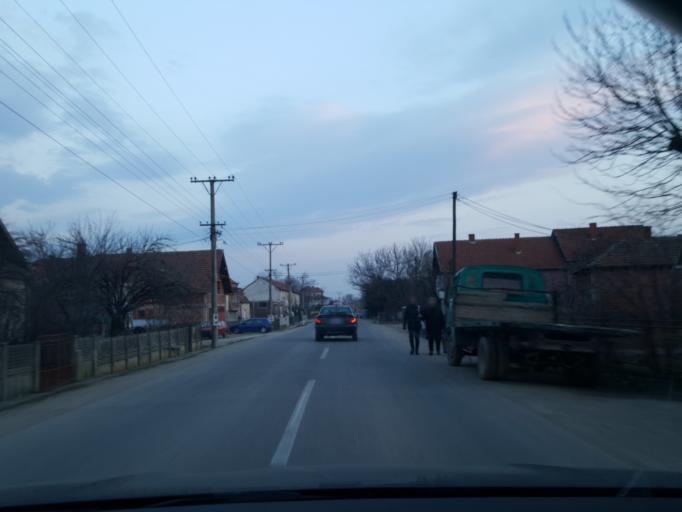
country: RS
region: Central Serbia
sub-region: Nisavski Okrug
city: Aleksinac
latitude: 43.5021
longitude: 21.7015
